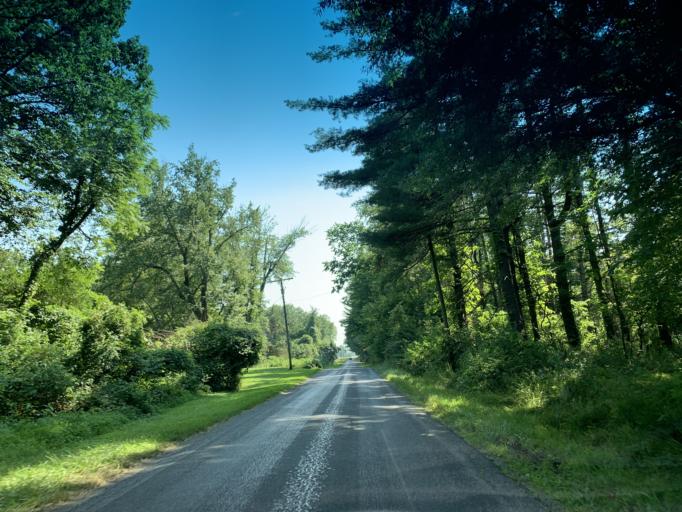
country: US
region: Maryland
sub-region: Montgomery County
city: Poolesville
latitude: 39.1150
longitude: -77.4604
